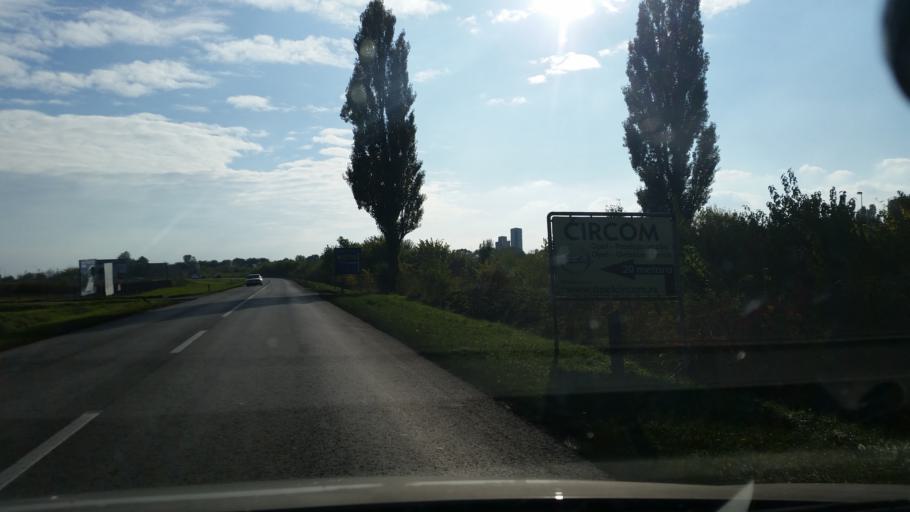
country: RS
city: Ecka
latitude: 45.3568
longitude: 20.4203
